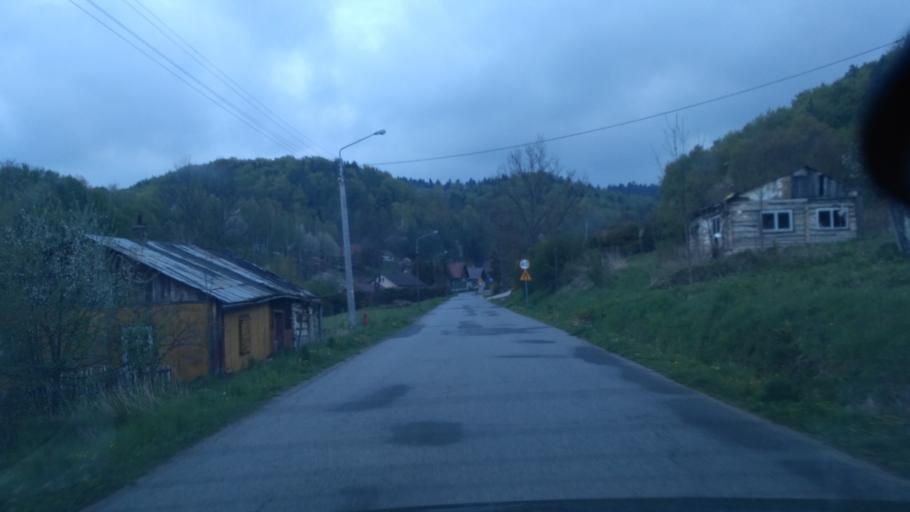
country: PL
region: Subcarpathian Voivodeship
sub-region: Powiat sanocki
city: Sanok
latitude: 49.5607
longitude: 22.2340
